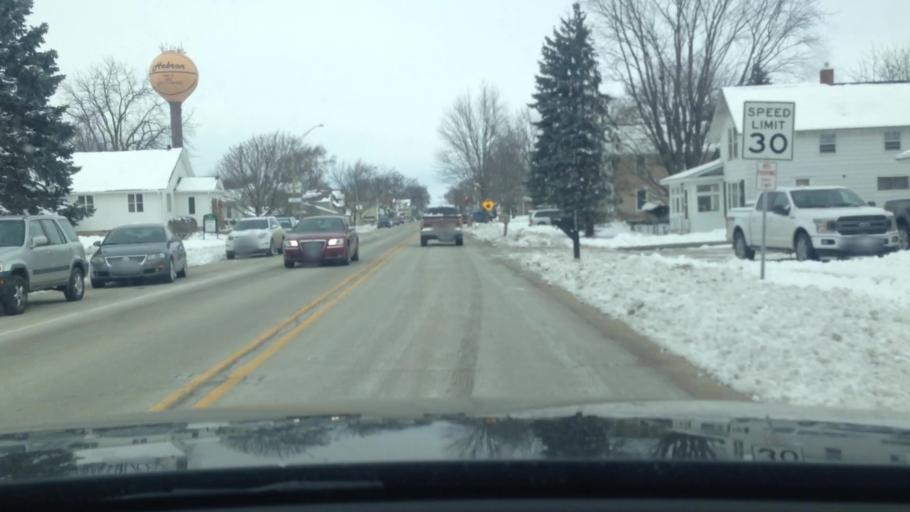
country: US
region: Illinois
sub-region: McHenry County
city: Hebron
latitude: 42.4689
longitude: -88.4327
